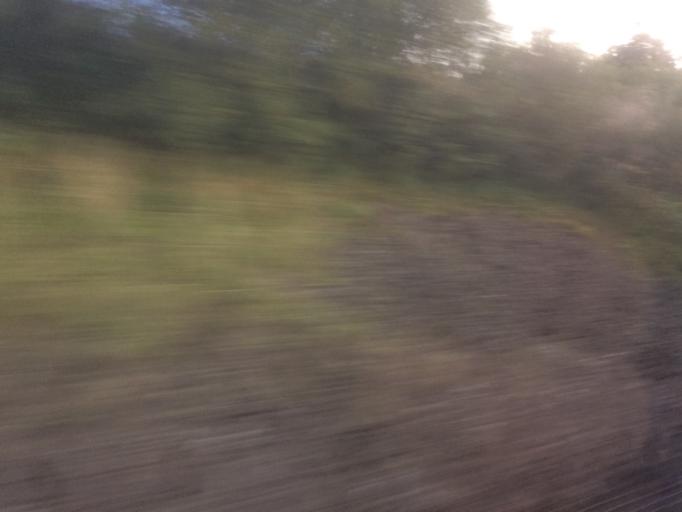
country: GB
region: Scotland
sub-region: North Lanarkshire
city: Cumbernauld
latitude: 55.9660
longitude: -4.0225
